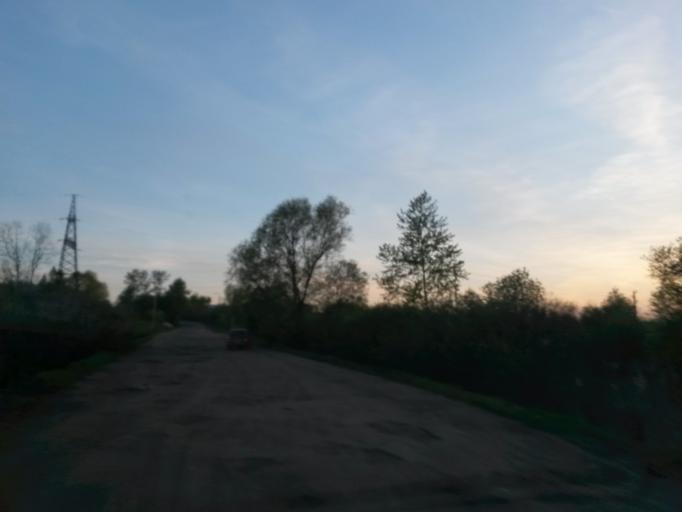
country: RU
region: Jaroslavl
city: Tutayev
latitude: 57.8927
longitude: 39.5612
